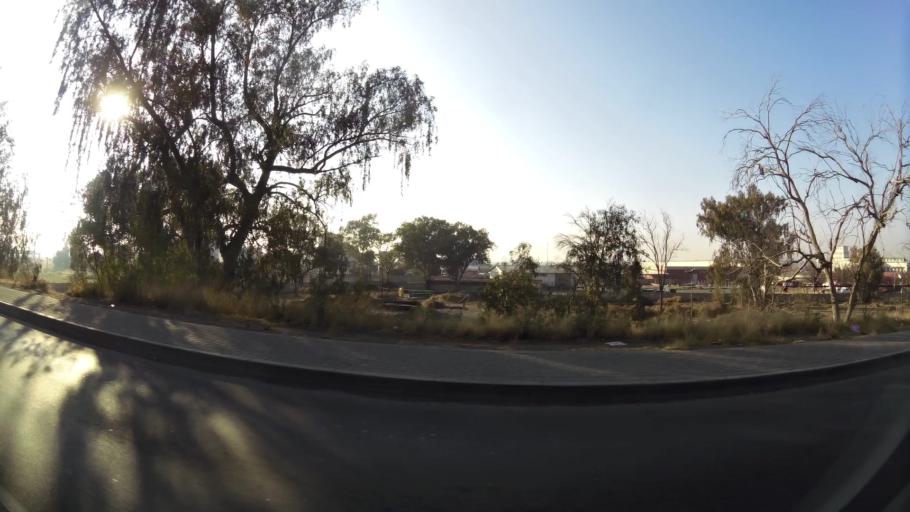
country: ZA
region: Orange Free State
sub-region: Mangaung Metropolitan Municipality
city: Bloemfontein
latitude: -29.1397
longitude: 26.2161
